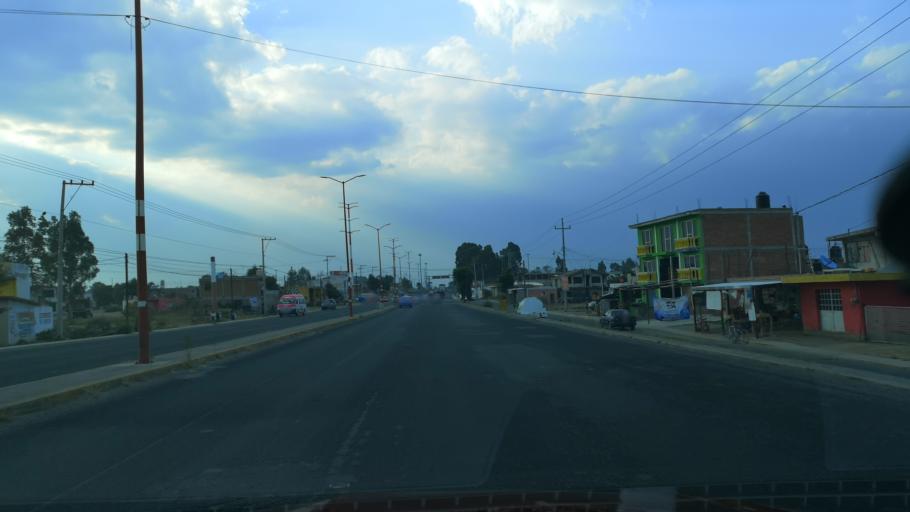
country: MX
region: Puebla
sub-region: Juan C. Bonilla
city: Santa Maria Zacatepec
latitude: 19.1265
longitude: -98.3684
